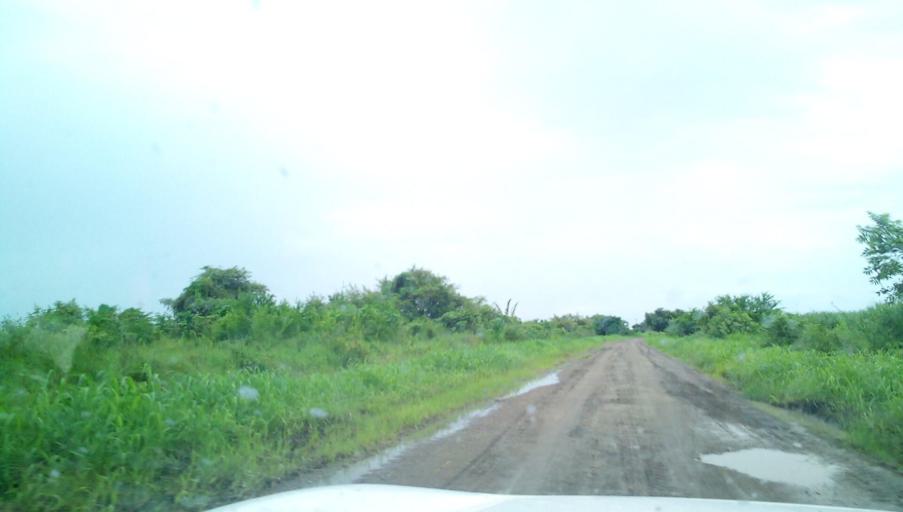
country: MX
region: Veracruz
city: Panuco
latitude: 21.8432
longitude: -98.1102
